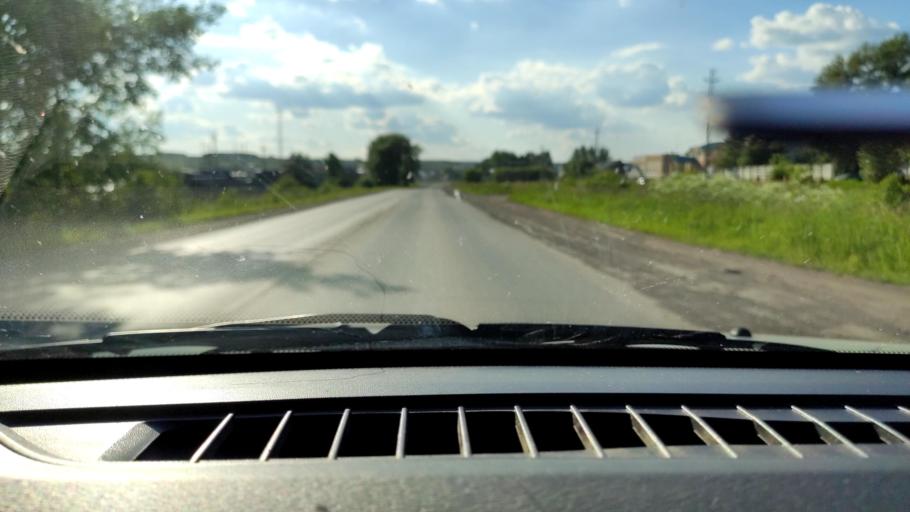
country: RU
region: Perm
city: Orda
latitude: 57.1887
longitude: 56.9118
